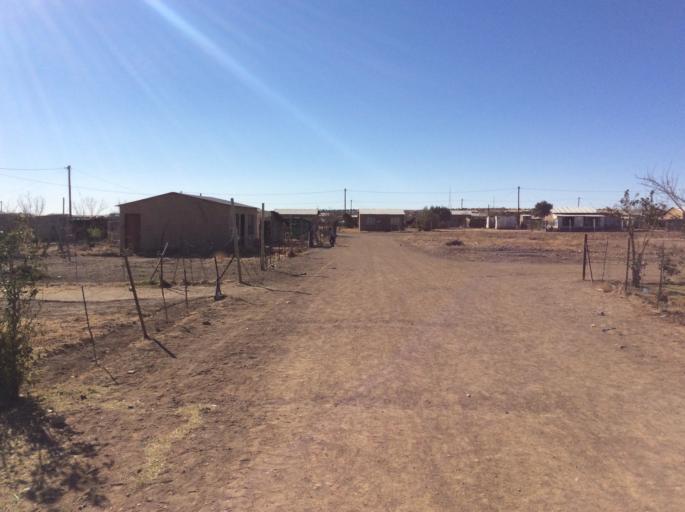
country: ZA
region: Orange Free State
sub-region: Lejweleputswa District Municipality
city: Brandfort
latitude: -28.7325
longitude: 26.1069
